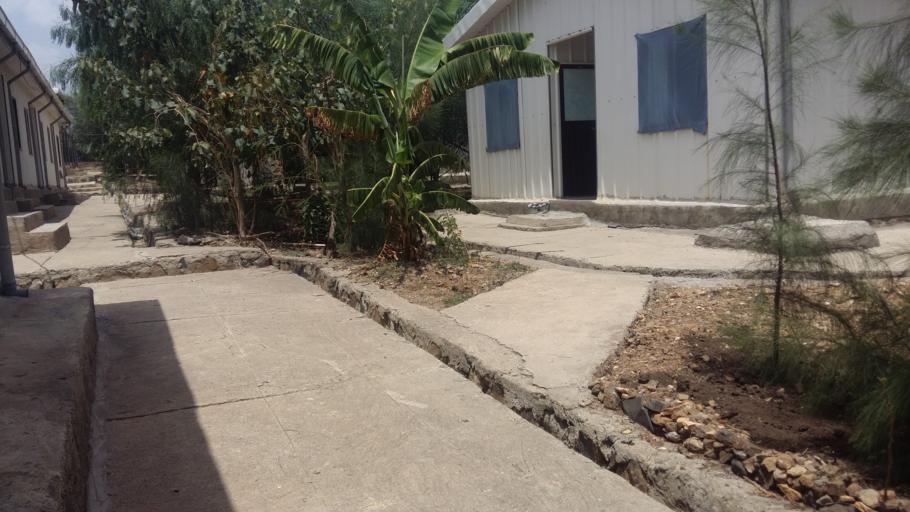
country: ET
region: Amhara
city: Were Ilu
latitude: 10.4222
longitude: 39.1146
